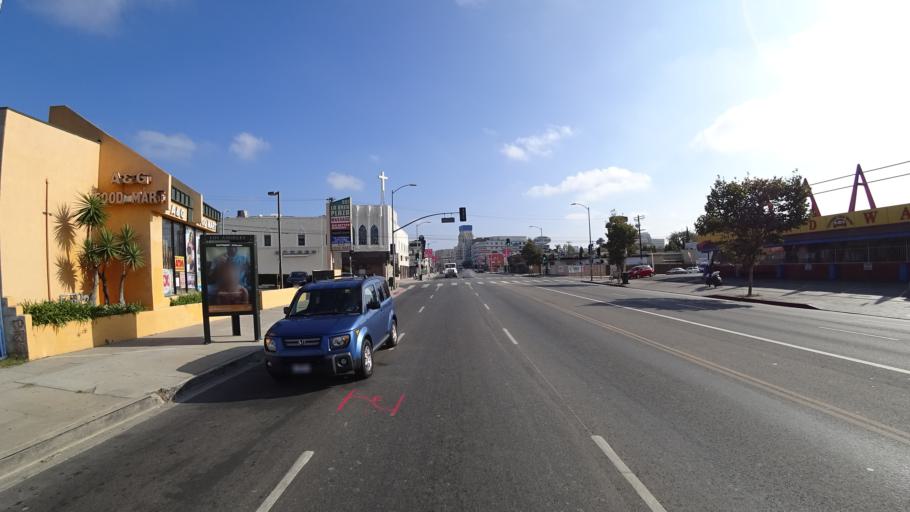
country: US
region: California
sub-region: Los Angeles County
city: West Hollywood
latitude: 34.0586
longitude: -118.3456
